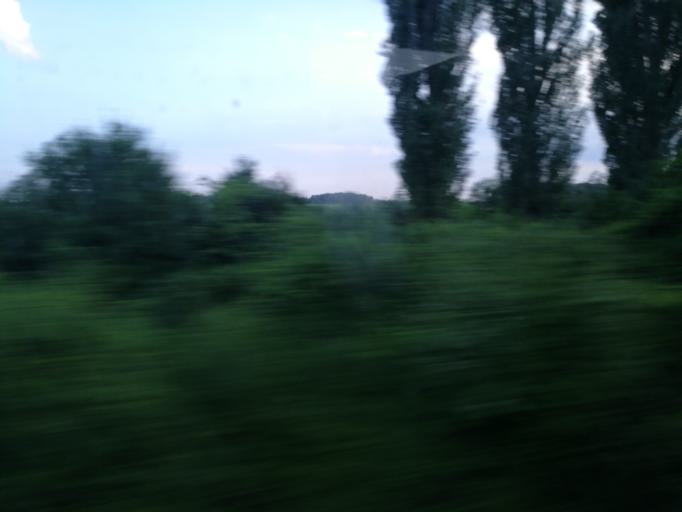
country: RO
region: Dambovita
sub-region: Comuna Contesti
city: Contesti
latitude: 44.6563
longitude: 25.6555
